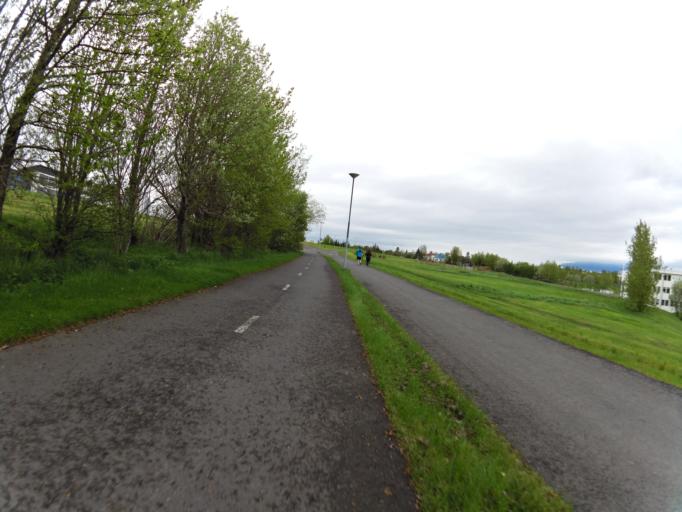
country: IS
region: Capital Region
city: Reykjavik
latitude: 64.1395
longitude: -21.8804
